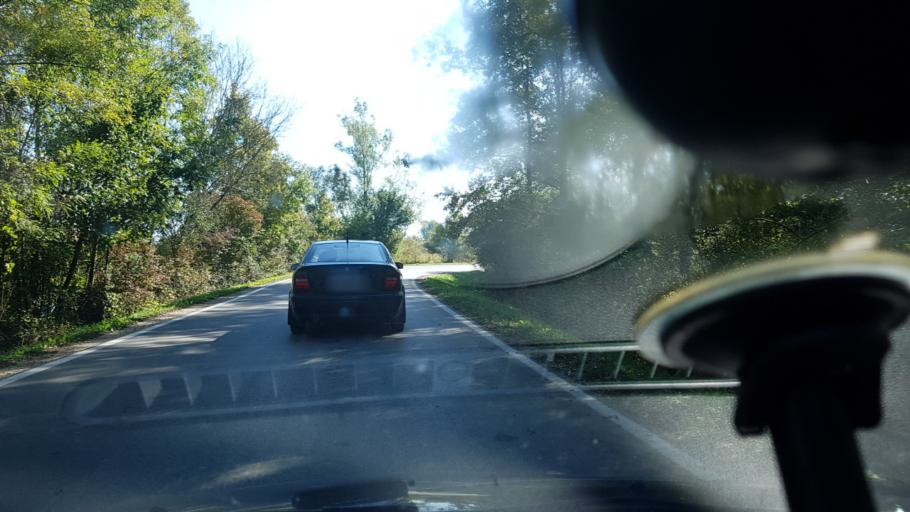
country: HR
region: Zagrebacka
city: Lupoglav
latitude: 45.7287
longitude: 16.3034
